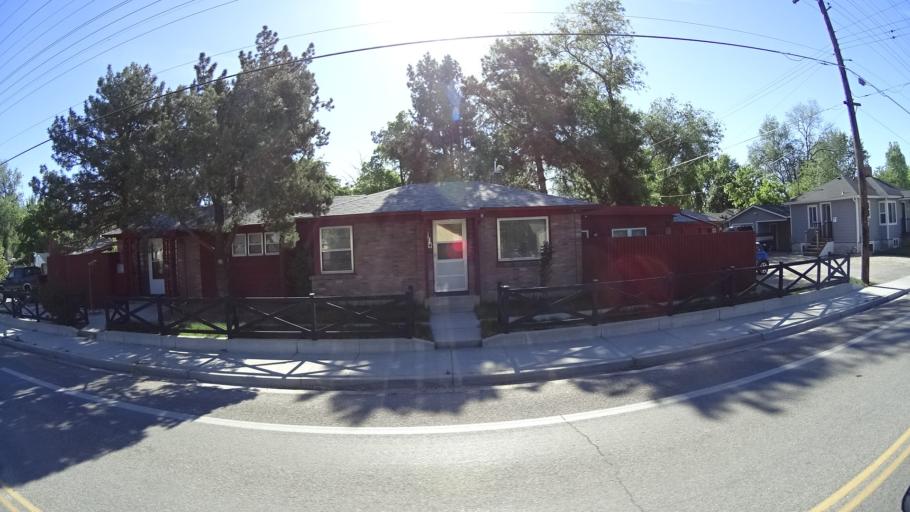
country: US
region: Idaho
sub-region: Ada County
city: Garden City
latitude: 43.6253
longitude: -116.2239
